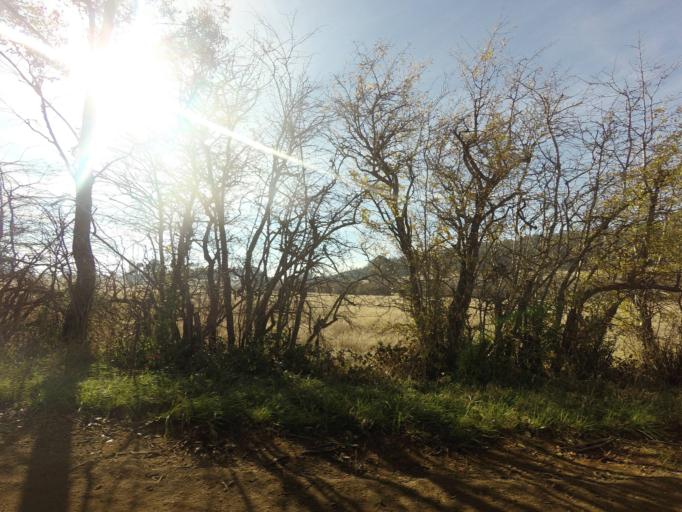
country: AU
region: Tasmania
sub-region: Sorell
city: Sorell
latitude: -42.4792
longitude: 147.4814
